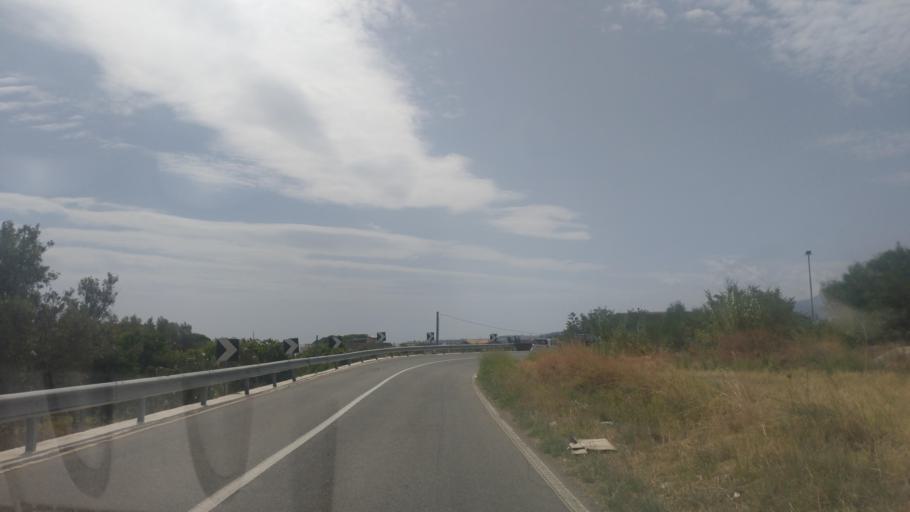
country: IT
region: Calabria
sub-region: Provincia di Catanzaro
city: Montepaone Lido
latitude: 38.7343
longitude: 16.5450
